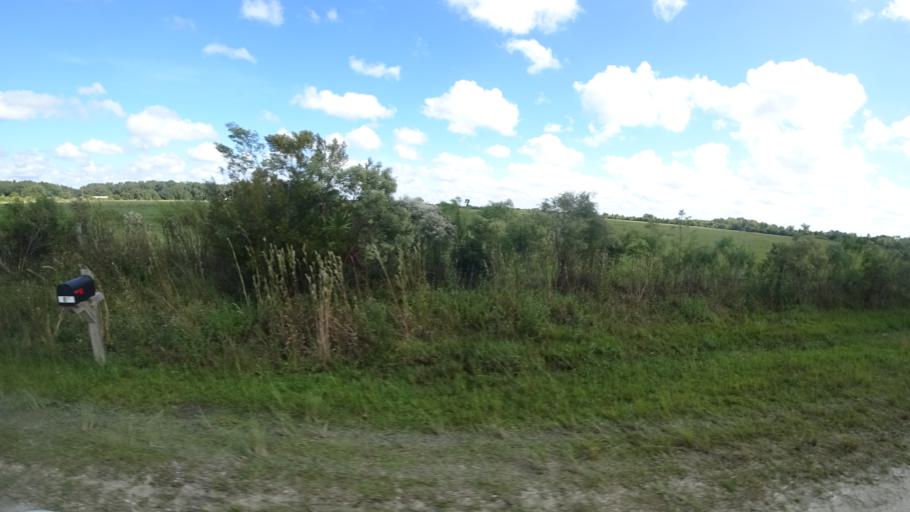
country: US
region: Florida
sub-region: Sarasota County
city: Lake Sarasota
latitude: 27.3645
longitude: -82.1353
